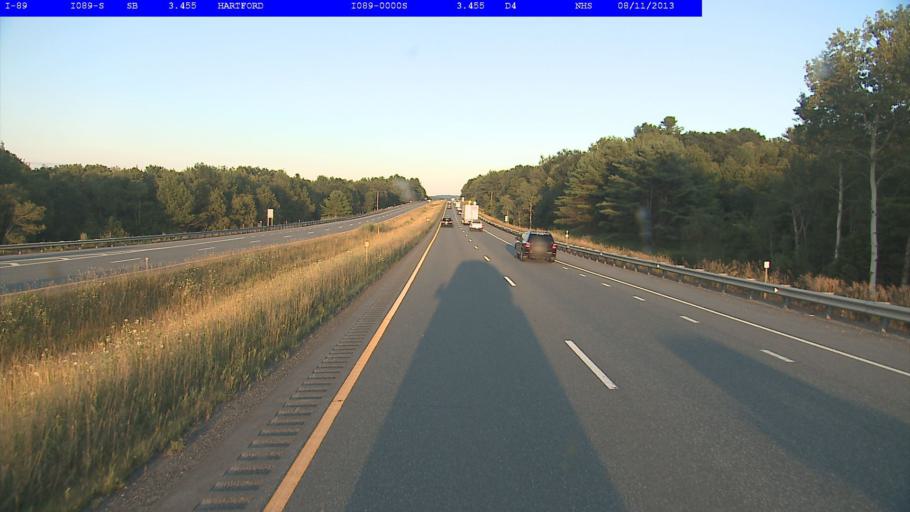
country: US
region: Vermont
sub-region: Windsor County
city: White River Junction
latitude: 43.6632
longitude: -72.3780
